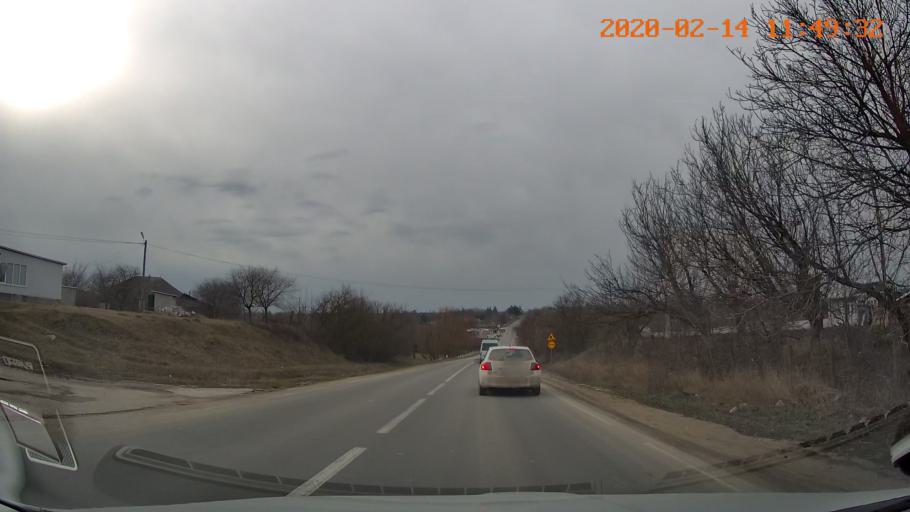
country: RO
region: Botosani
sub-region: Comuna Radauti-Prut
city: Miorcani
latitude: 48.2993
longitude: 26.9395
